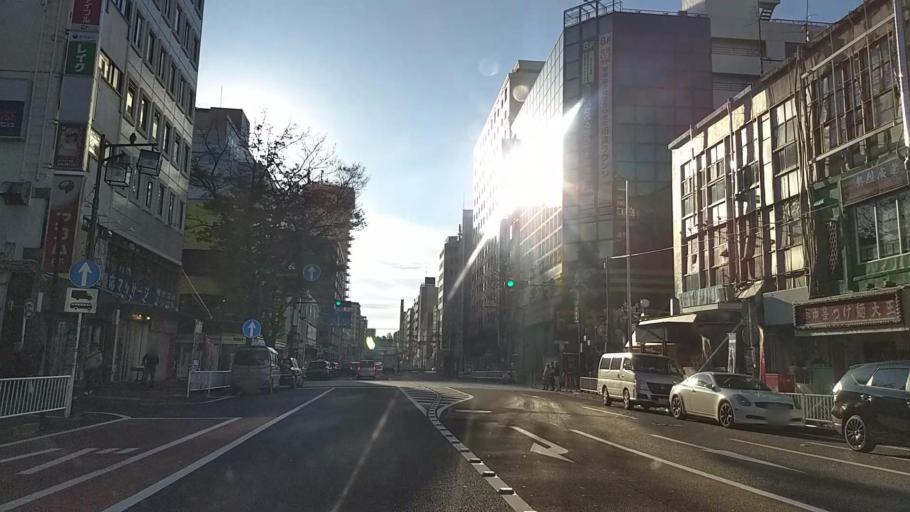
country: JP
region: Kanagawa
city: Yokohama
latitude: 35.4431
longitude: 139.6305
